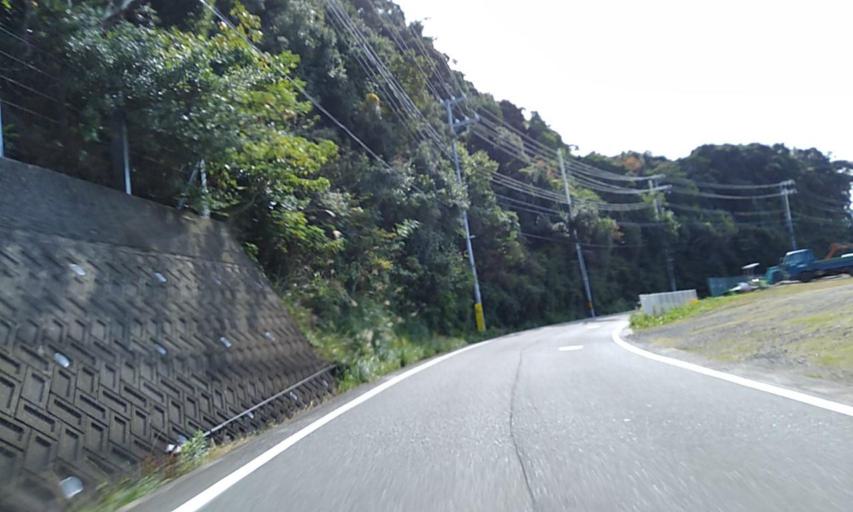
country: JP
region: Wakayama
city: Gobo
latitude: 33.9660
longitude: 135.1029
